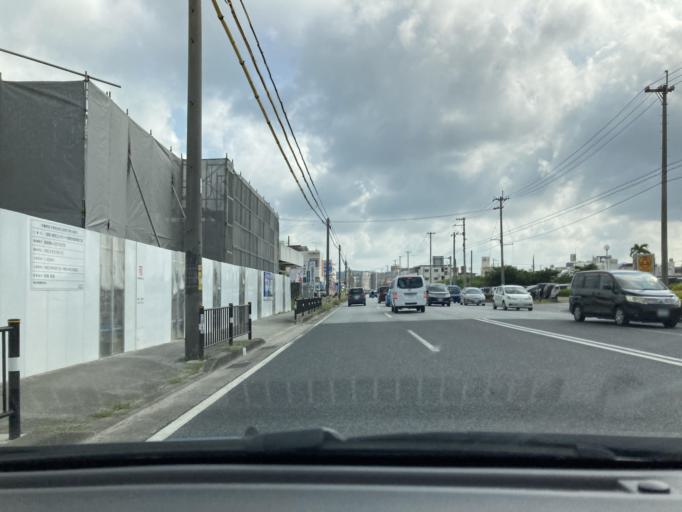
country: JP
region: Okinawa
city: Ginowan
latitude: 26.2245
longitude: 127.7658
